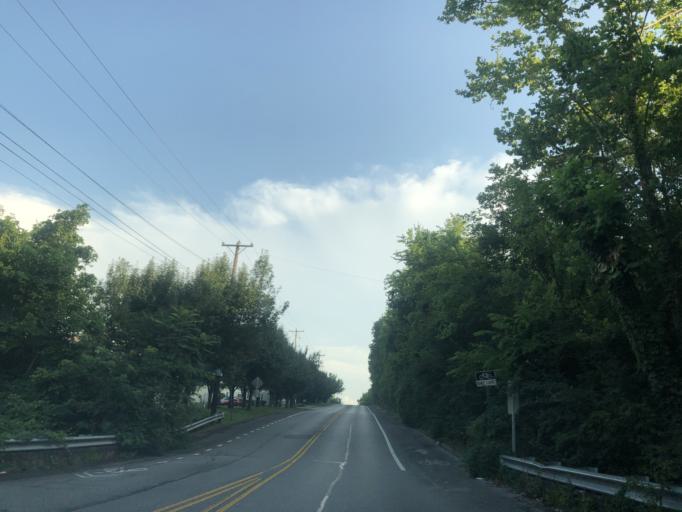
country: US
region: Tennessee
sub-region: Davidson County
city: Lakewood
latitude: 36.1411
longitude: -86.6408
